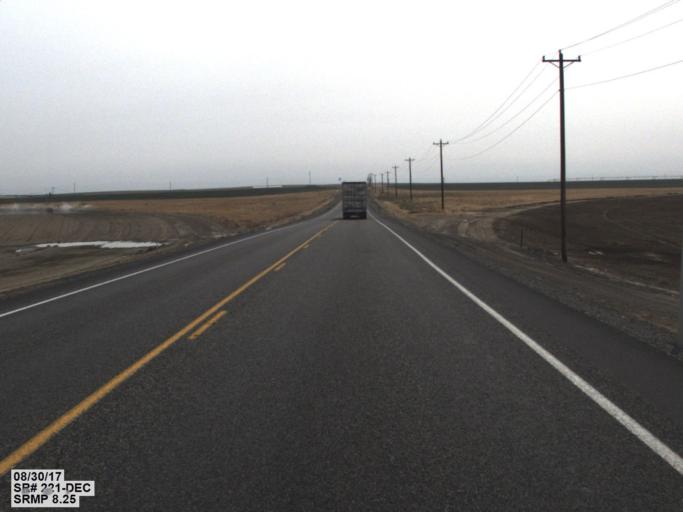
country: US
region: Oregon
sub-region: Morrow County
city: Irrigon
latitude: 46.0546
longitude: -119.6022
